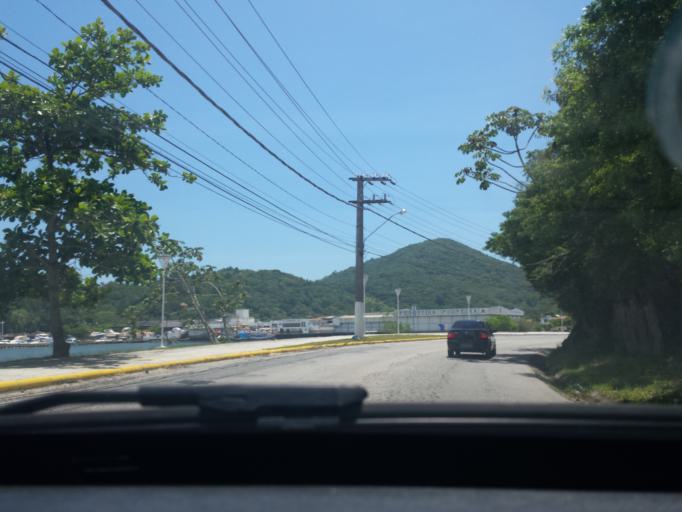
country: BR
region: Santa Catarina
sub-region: Porto Belo
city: Porto Belo
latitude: -27.1477
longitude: -48.5346
